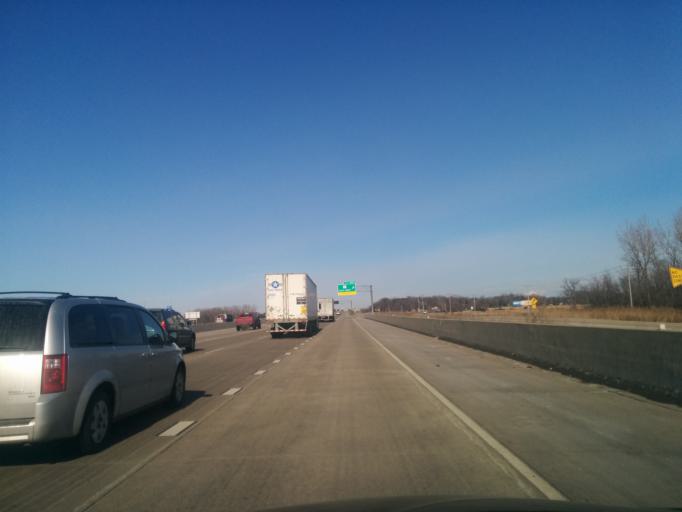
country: US
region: Wisconsin
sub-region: Kenosha County
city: Pleasant Prairie
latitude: 42.5376
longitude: -87.9520
